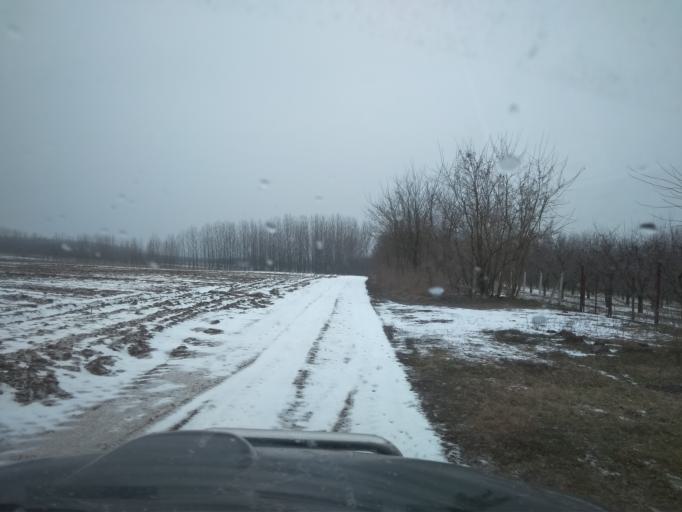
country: HU
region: Szabolcs-Szatmar-Bereg
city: Apagy
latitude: 47.9777
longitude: 21.9142
